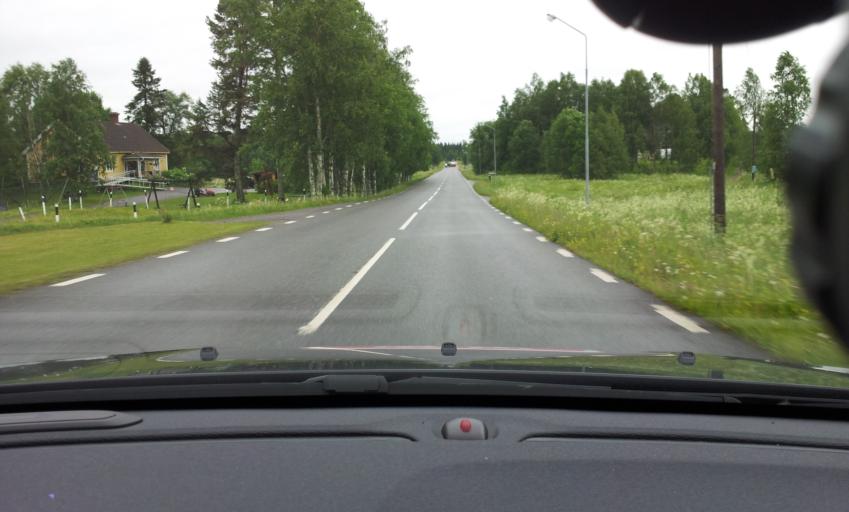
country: SE
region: Jaemtland
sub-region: Stroemsunds Kommun
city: Stroemsund
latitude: 63.5547
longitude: 15.4035
